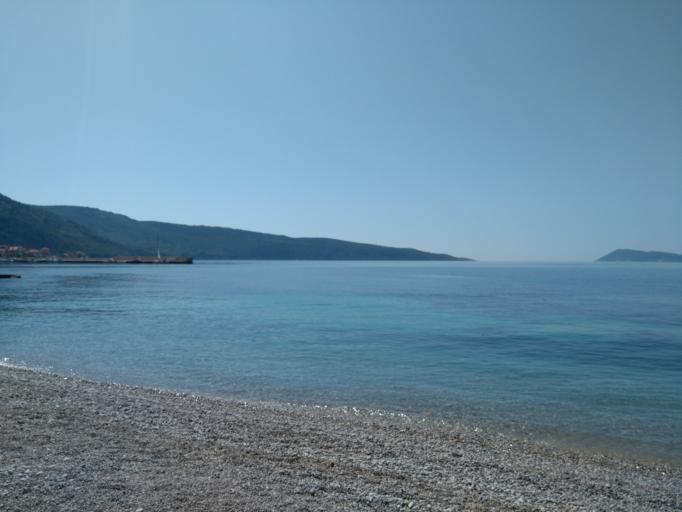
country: HR
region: Splitsko-Dalmatinska
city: Komiza
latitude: 43.0479
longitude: 16.0849
